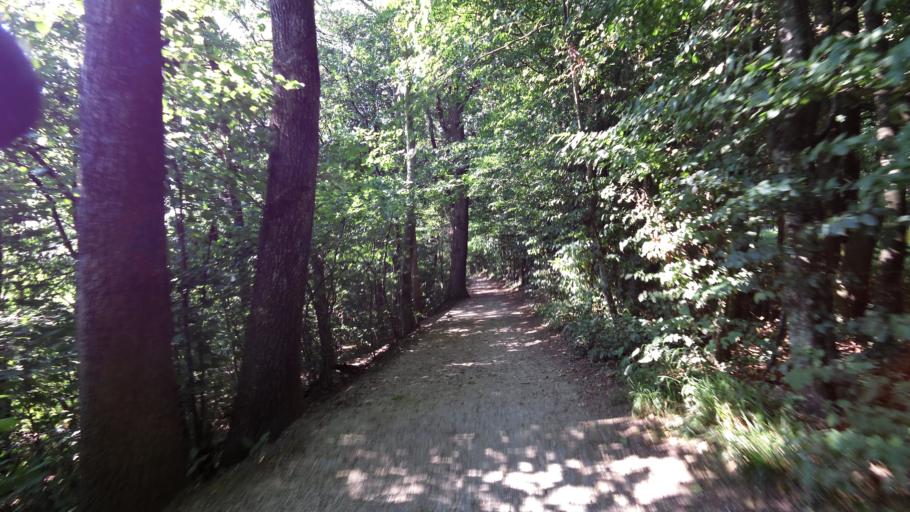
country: DE
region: Bavaria
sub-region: Upper Bavaria
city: Chieming
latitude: 47.8994
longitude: 12.5250
